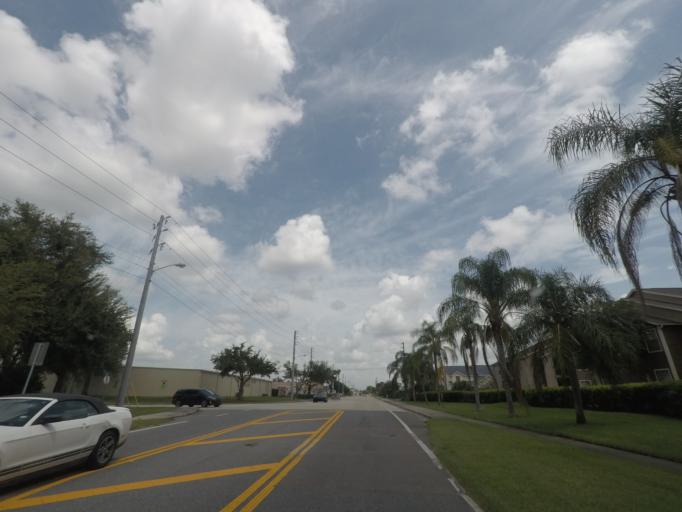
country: US
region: Florida
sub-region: Osceola County
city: Kissimmee
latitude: 28.2995
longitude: -81.4368
